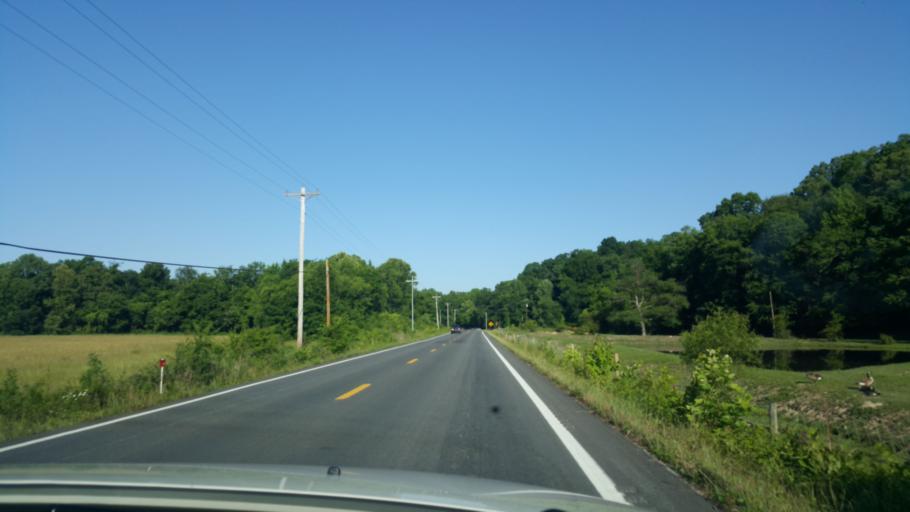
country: US
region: Tennessee
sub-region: Lawrence County
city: Lawrenceburg
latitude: 35.3988
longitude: -87.3805
